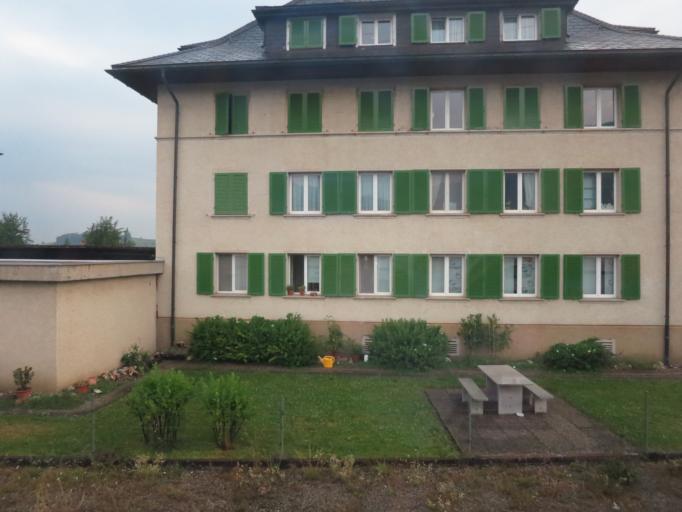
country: CH
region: Schwyz
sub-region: Bezirk March
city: Schubelbach
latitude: 47.1829
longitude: 8.9012
